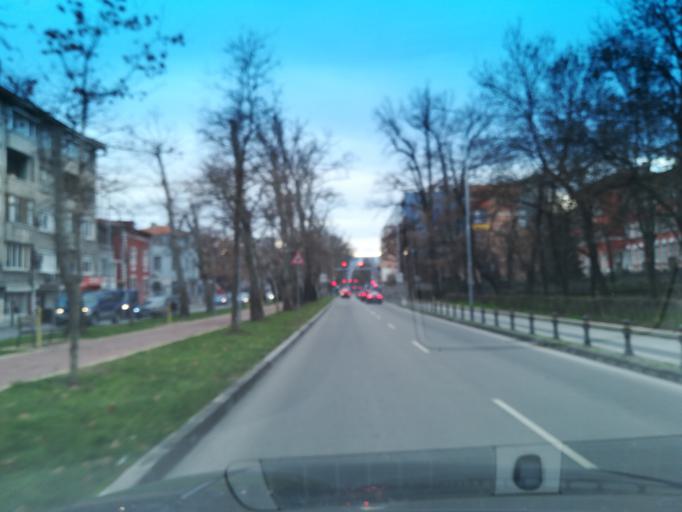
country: BG
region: Plovdiv
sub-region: Obshtina Plovdiv
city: Plovdiv
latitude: 42.1433
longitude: 24.7413
